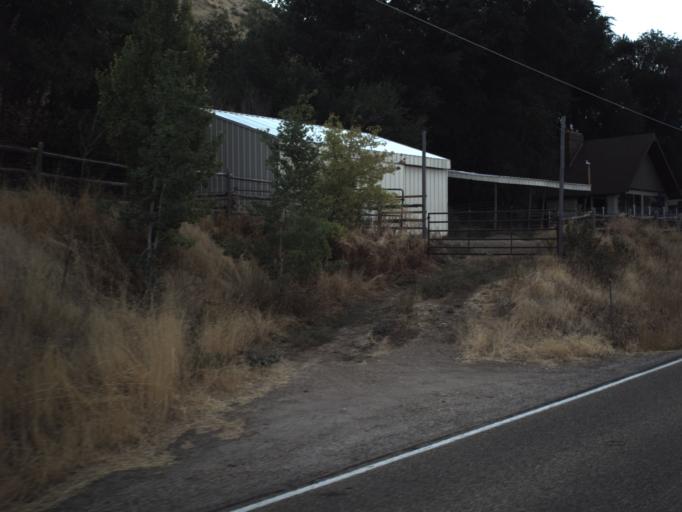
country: US
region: Utah
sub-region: Morgan County
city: Morgan
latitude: 41.0237
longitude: -111.6751
